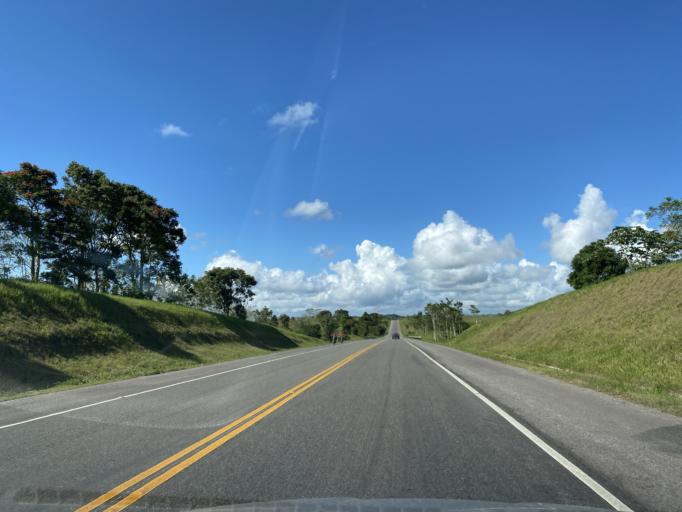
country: DO
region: Monte Plata
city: Majagual
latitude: 18.9956
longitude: -69.8161
